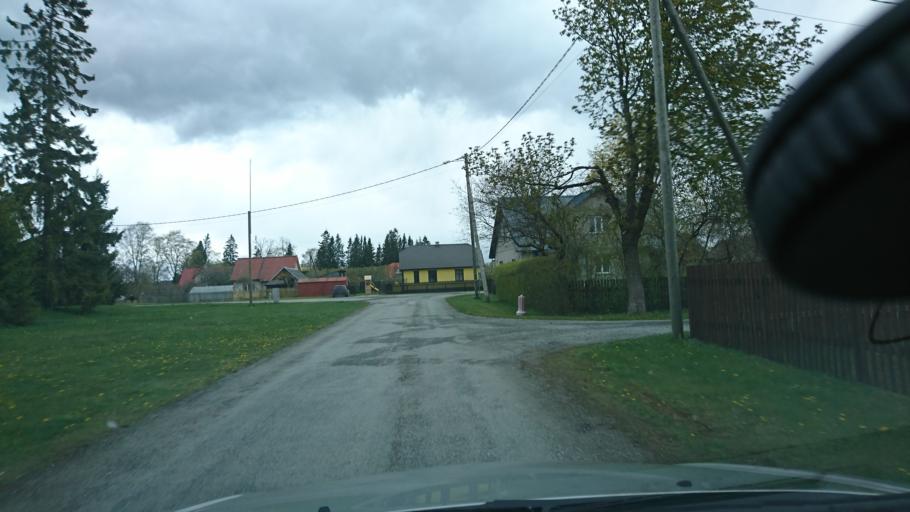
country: EE
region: Laeaene-Virumaa
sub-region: Tapa vald
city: Tapa
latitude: 59.2569
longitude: 25.9669
